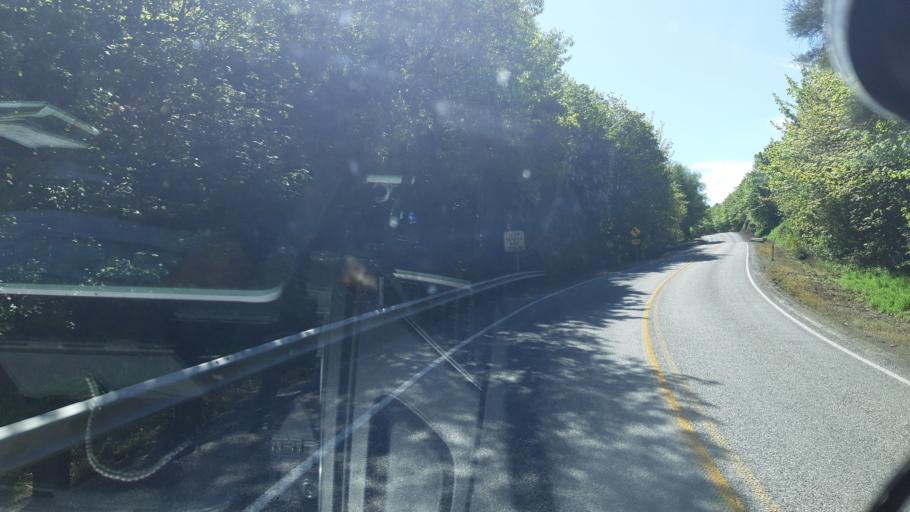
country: NZ
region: Otago
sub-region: Clutha District
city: Milton
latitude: -46.0693
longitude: 169.8294
